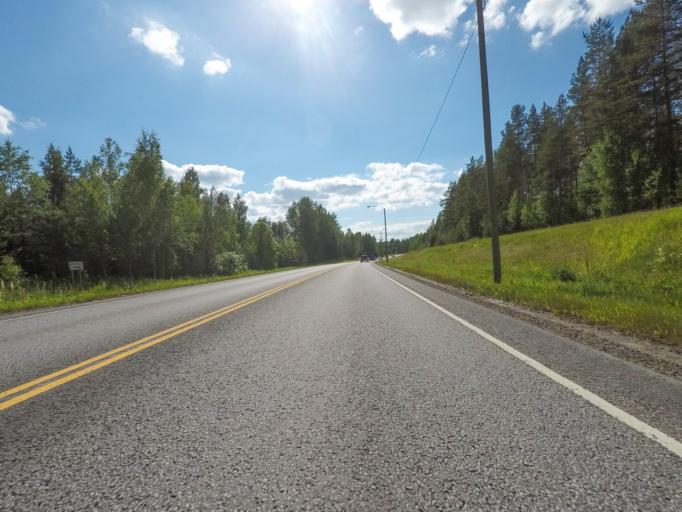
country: FI
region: Southern Savonia
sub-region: Savonlinna
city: Savonlinna
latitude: 61.8780
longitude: 29.0094
